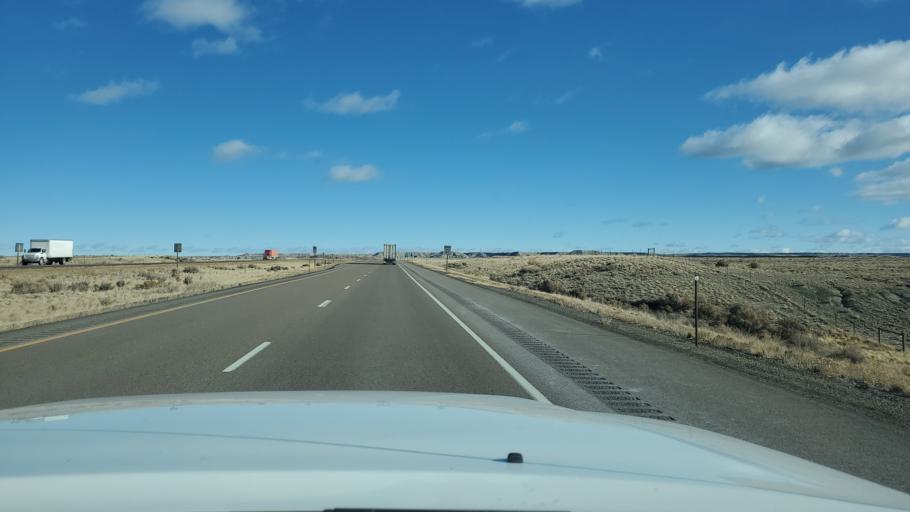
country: US
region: Wyoming
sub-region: Uinta County
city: Lyman
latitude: 41.3891
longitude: -110.1994
